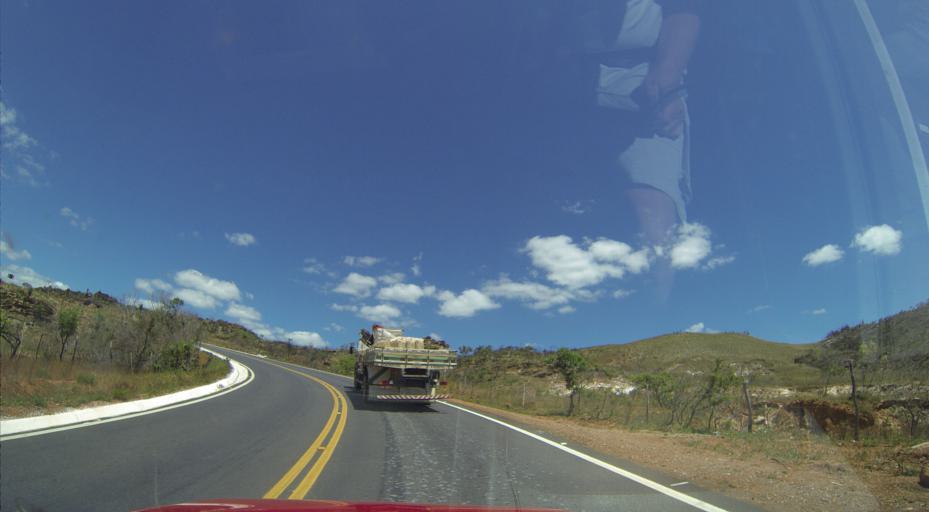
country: BR
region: Minas Gerais
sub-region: Conceicao Do Mato Dentro
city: Conceicao do Mato Dentro
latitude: -19.2857
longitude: -43.5762
